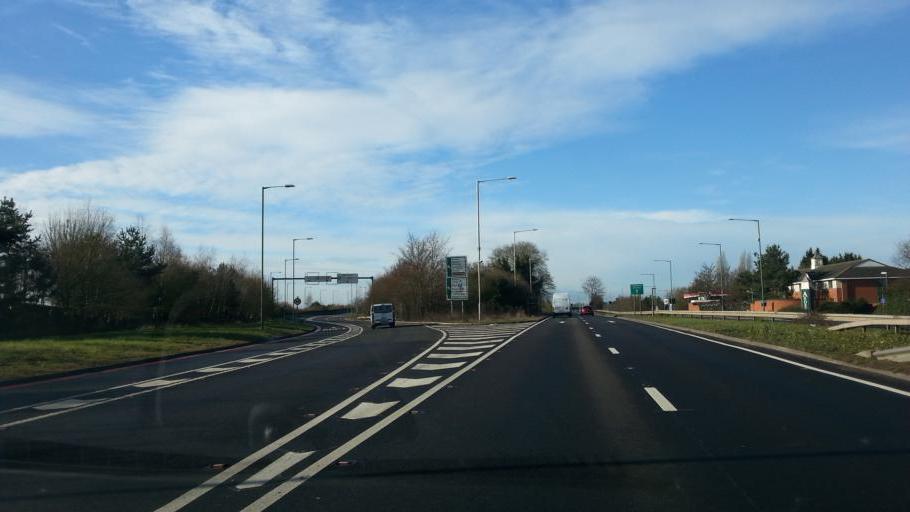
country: GB
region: England
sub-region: Solihull
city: Bickenhill
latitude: 52.4446
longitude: -1.7189
